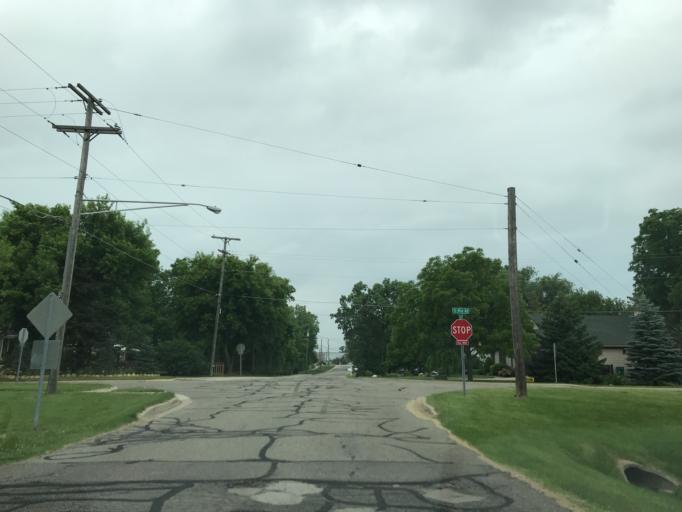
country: US
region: Michigan
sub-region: Oakland County
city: Novi
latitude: 42.4804
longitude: -83.4843
